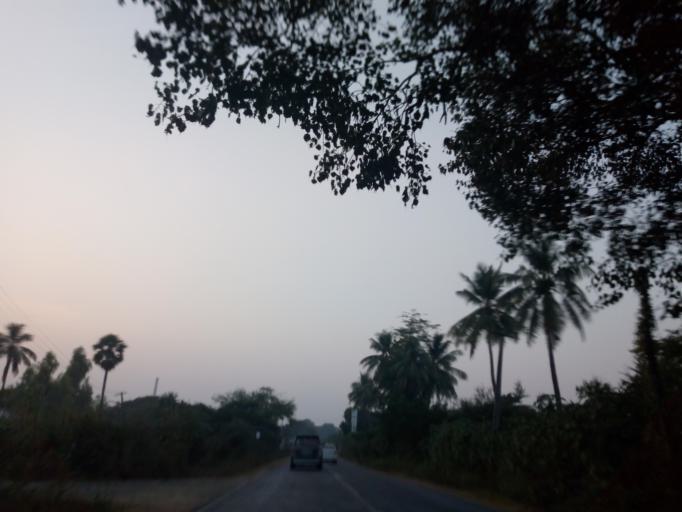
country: IN
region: Andhra Pradesh
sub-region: West Godavari
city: Tadepallegudem
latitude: 16.8180
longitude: 81.4903
